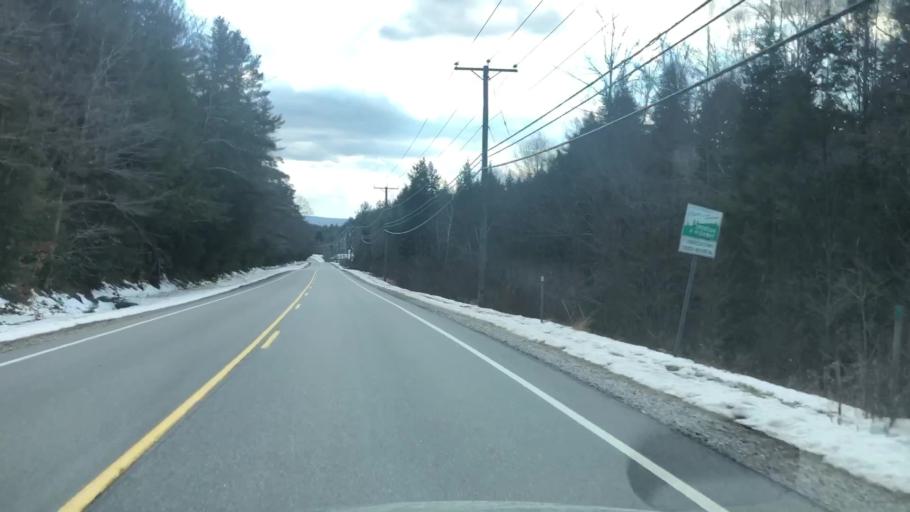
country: US
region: New Hampshire
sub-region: Hillsborough County
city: Mont Vernon
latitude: 42.8687
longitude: -71.6695
